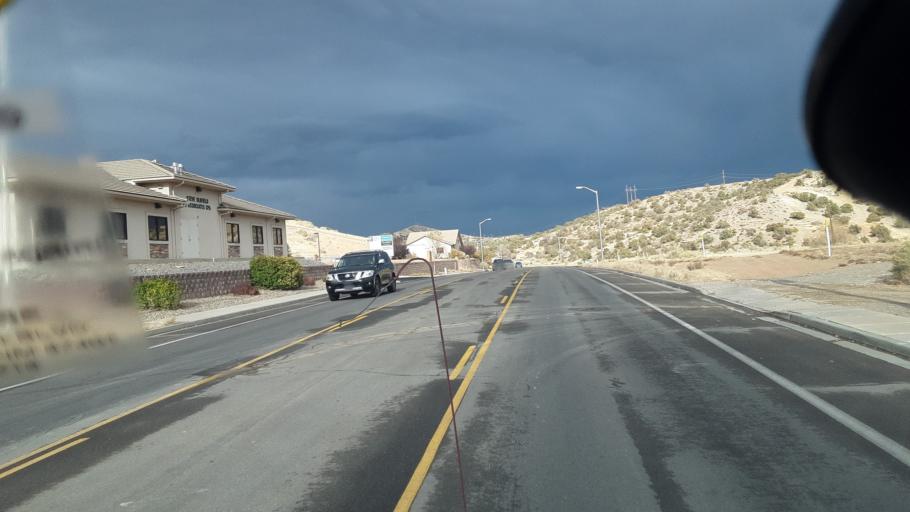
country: US
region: New Mexico
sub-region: San Juan County
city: Farmington
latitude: 36.7631
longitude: -108.1889
